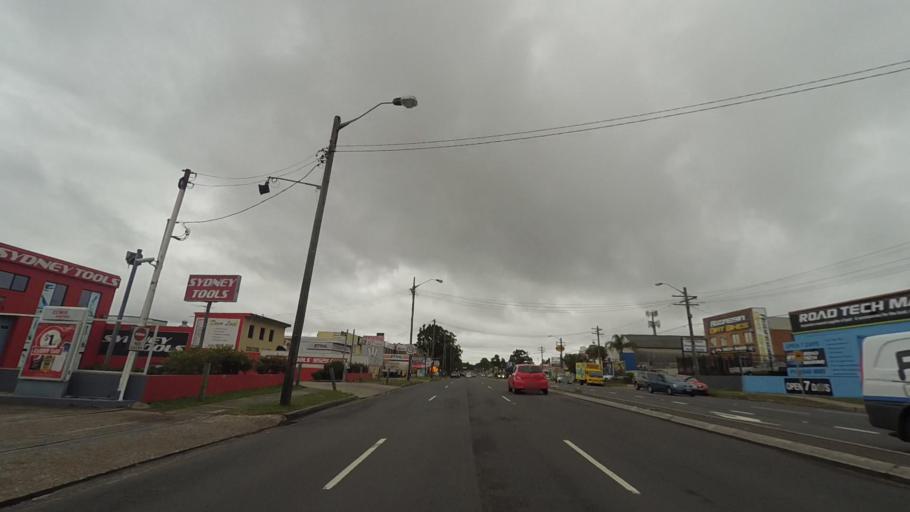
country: AU
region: New South Wales
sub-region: Sutherland Shire
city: Caringbah
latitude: -34.0263
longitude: 151.1204
